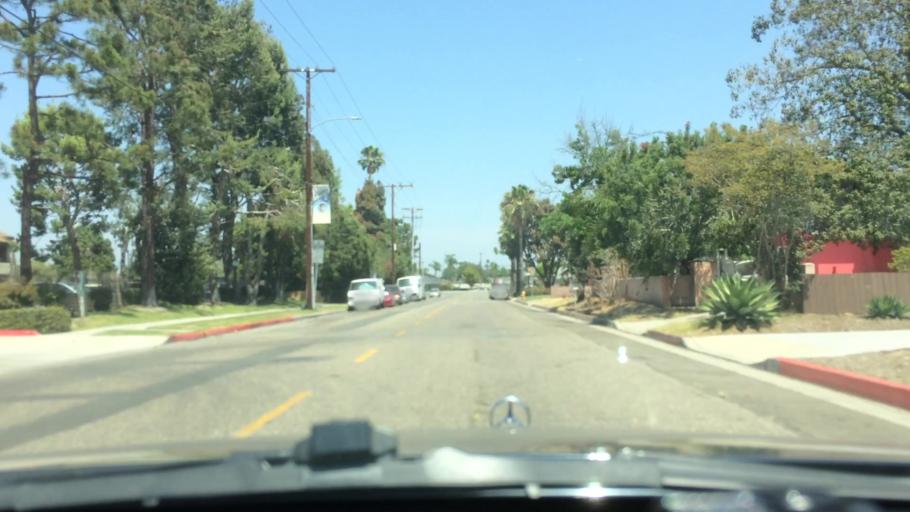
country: US
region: California
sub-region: Orange County
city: Anaheim
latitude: 33.8454
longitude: -117.8914
